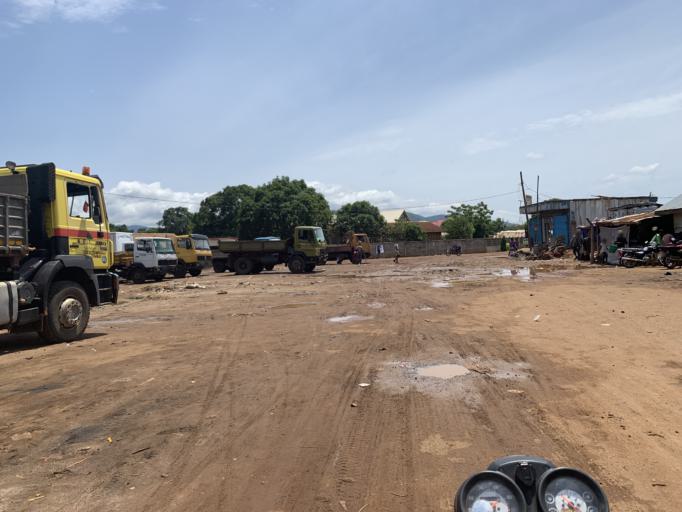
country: SL
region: Western Area
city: Waterloo
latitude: 8.3360
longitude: -13.0419
